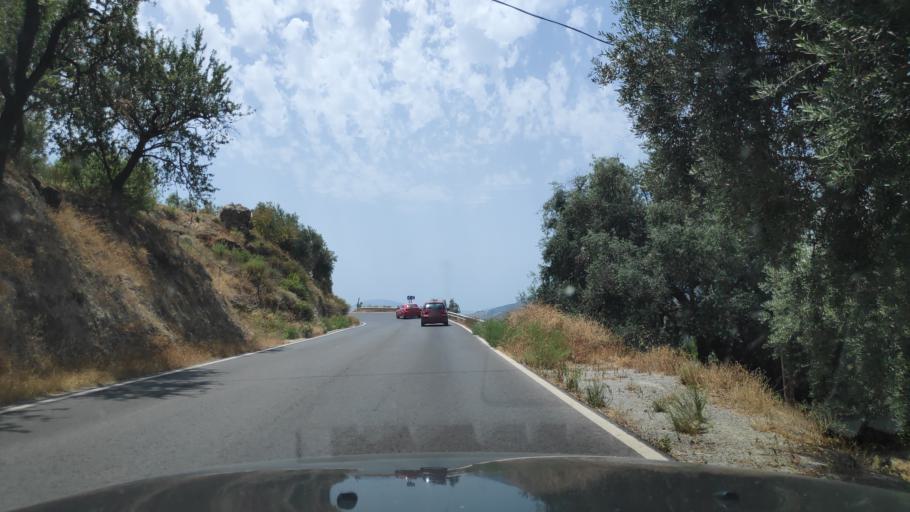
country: ES
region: Andalusia
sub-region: Provincia de Granada
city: Lanjaron
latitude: 36.9101
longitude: -3.4708
